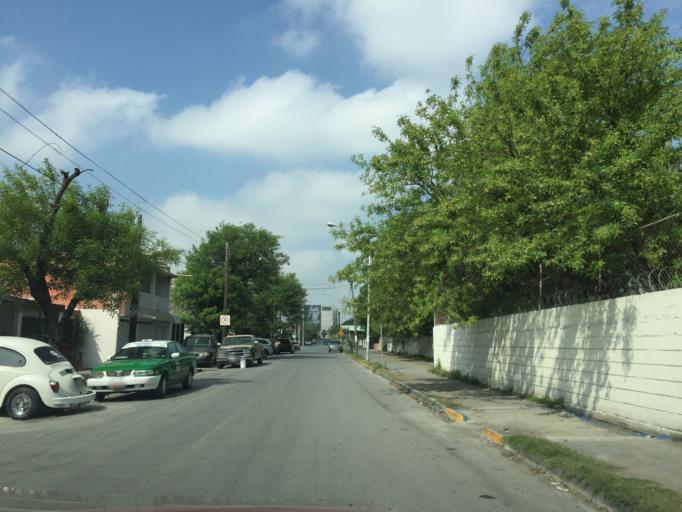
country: MX
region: Nuevo Leon
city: Guadalupe
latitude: 25.7063
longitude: -100.2200
